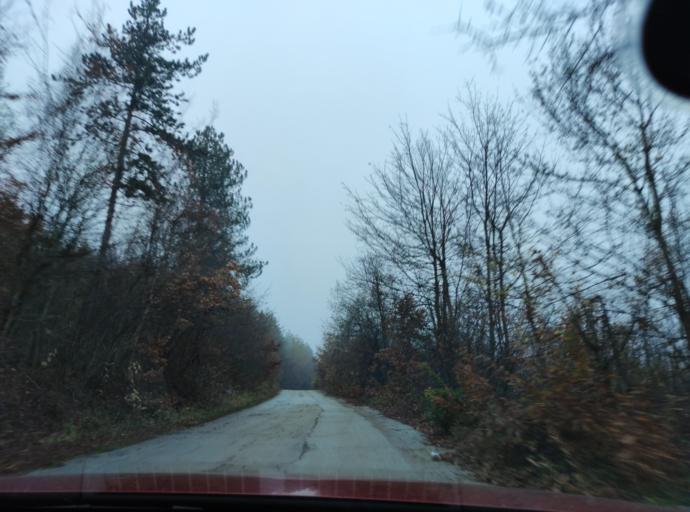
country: BG
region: Lovech
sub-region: Obshtina Yablanitsa
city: Yablanitsa
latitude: 43.1076
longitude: 24.0687
